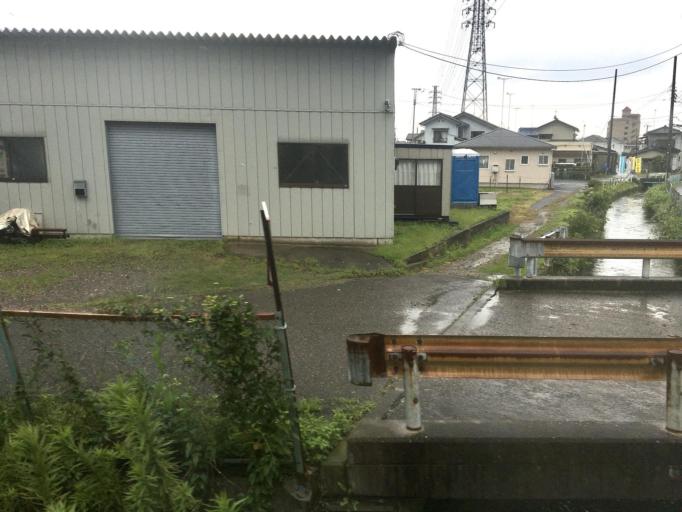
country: JP
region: Tochigi
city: Ashikaga
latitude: 36.3119
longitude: 139.4560
